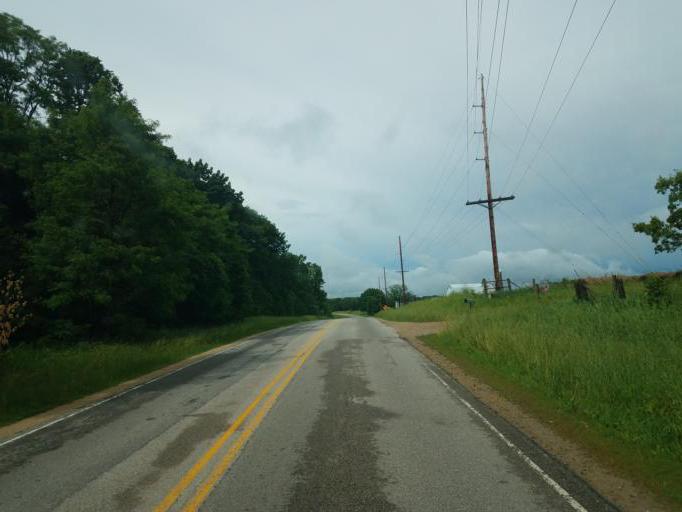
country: US
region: Wisconsin
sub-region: Vernon County
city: Hillsboro
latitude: 43.6748
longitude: -90.4560
